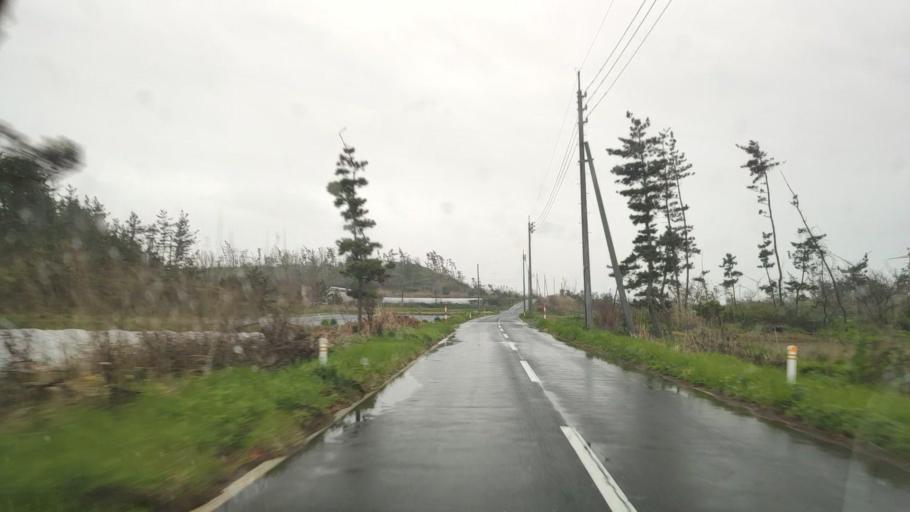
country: JP
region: Akita
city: Noshiromachi
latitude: 40.0913
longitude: 139.9612
